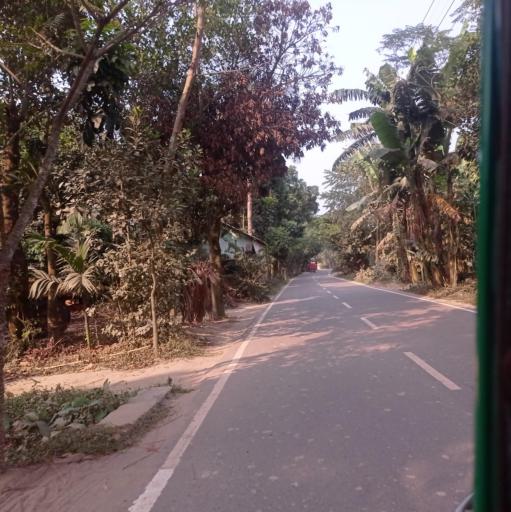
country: BD
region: Dhaka
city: Bhairab Bazar
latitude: 24.0900
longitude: 90.8499
